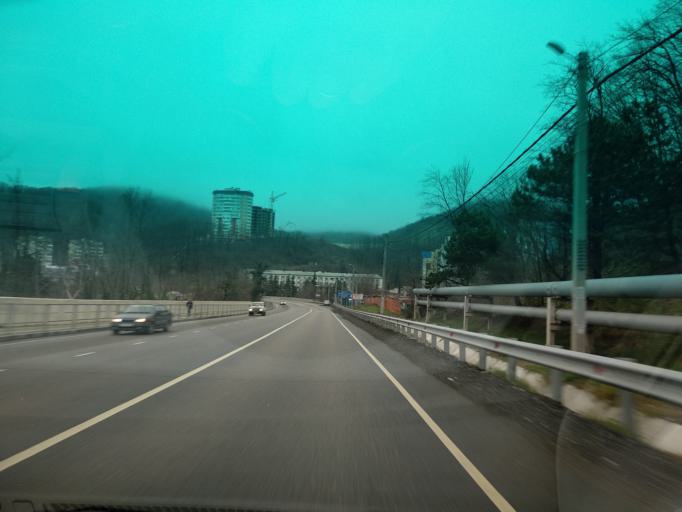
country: RU
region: Krasnodarskiy
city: Tuapse
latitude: 44.1146
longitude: 39.0693
